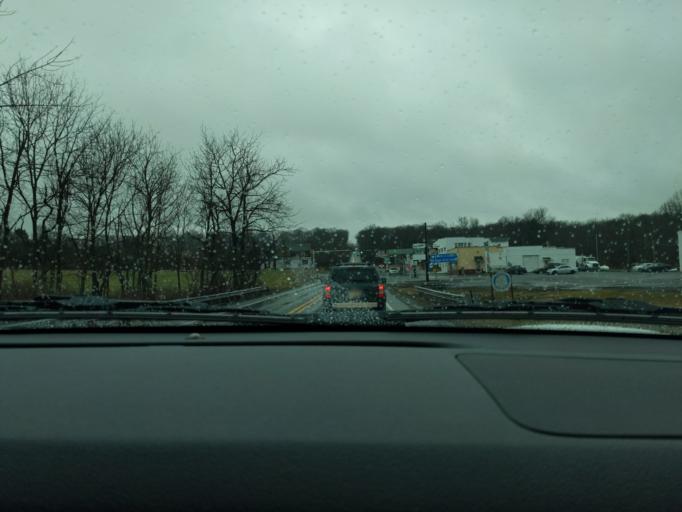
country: US
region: Pennsylvania
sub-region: Bucks County
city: Perkasie
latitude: 40.4028
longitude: -75.2525
